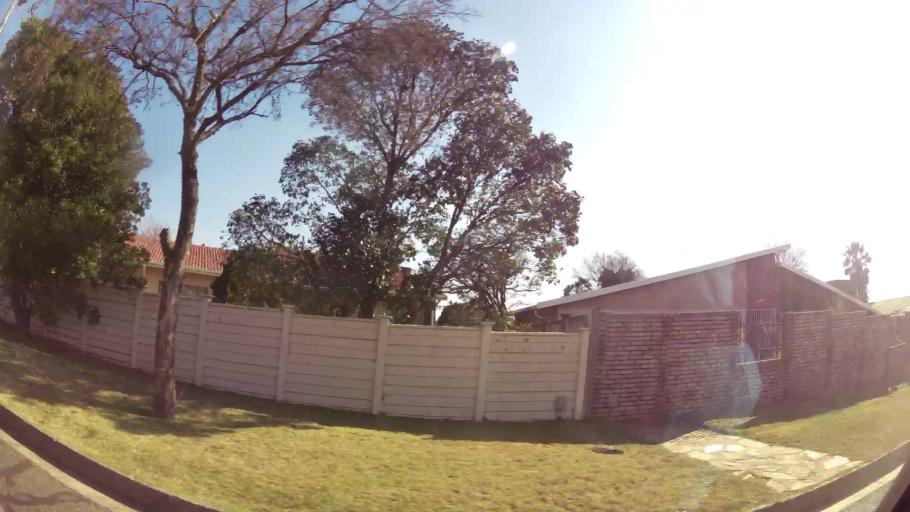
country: ZA
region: Gauteng
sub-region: City of Johannesburg Metropolitan Municipality
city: Johannesburg
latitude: -26.2565
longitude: 27.9962
